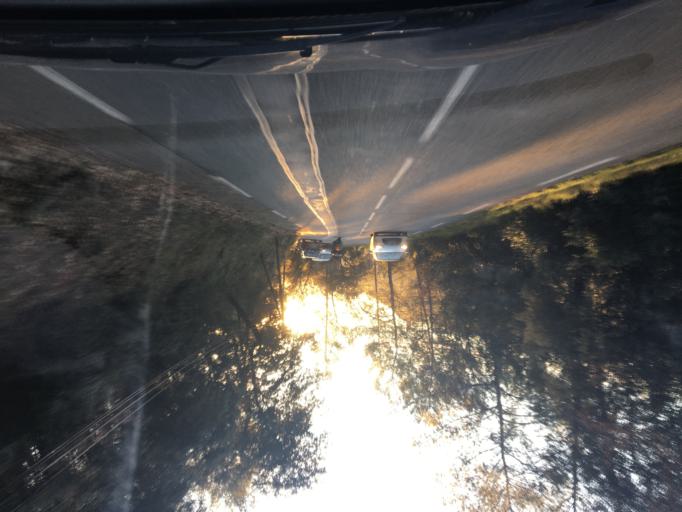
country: FR
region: Provence-Alpes-Cote d'Azur
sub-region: Departement du Var
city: Taradeau
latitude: 43.4569
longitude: 6.4200
